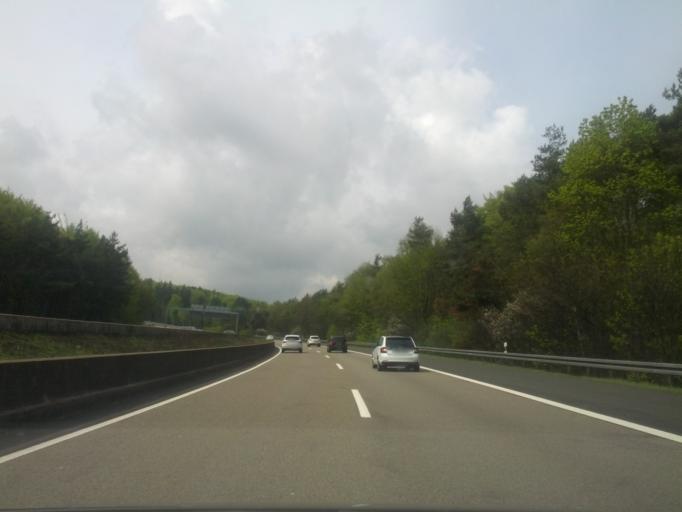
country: DE
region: Hesse
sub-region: Regierungsbezirk Kassel
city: Kirchheim
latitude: 50.8081
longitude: 9.5139
